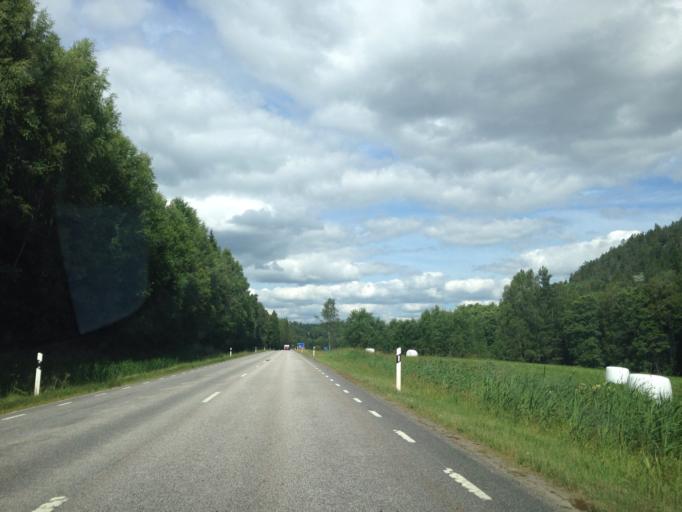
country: SE
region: OEstergoetland
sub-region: Kinda Kommun
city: Kisa
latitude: 57.9709
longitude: 15.6494
